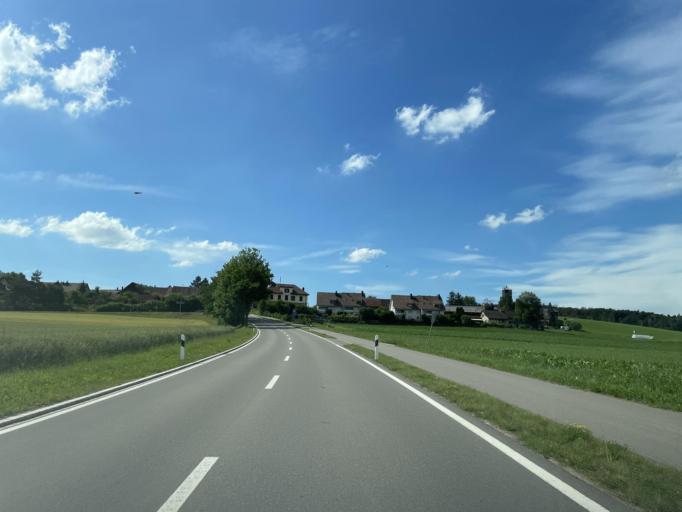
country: CH
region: Zurich
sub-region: Bezirk Winterthur
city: Hettlingen
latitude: 47.5401
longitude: 8.6837
